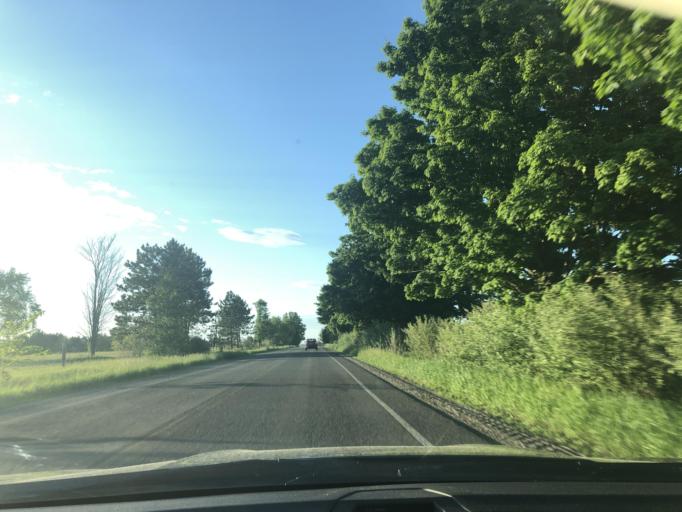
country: US
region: Michigan
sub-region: Missaukee County
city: Lake City
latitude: 44.4048
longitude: -85.0756
